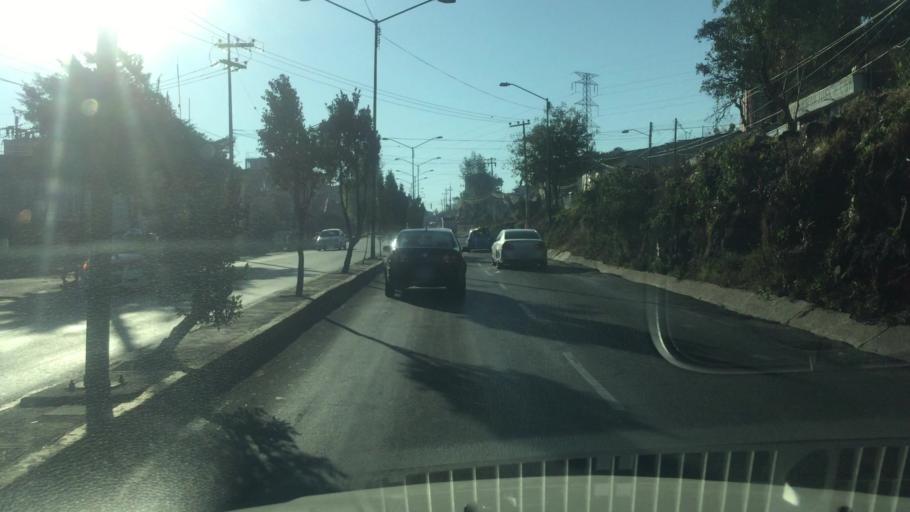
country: MX
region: Mexico City
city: Tlalpan
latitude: 19.2762
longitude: -99.2086
